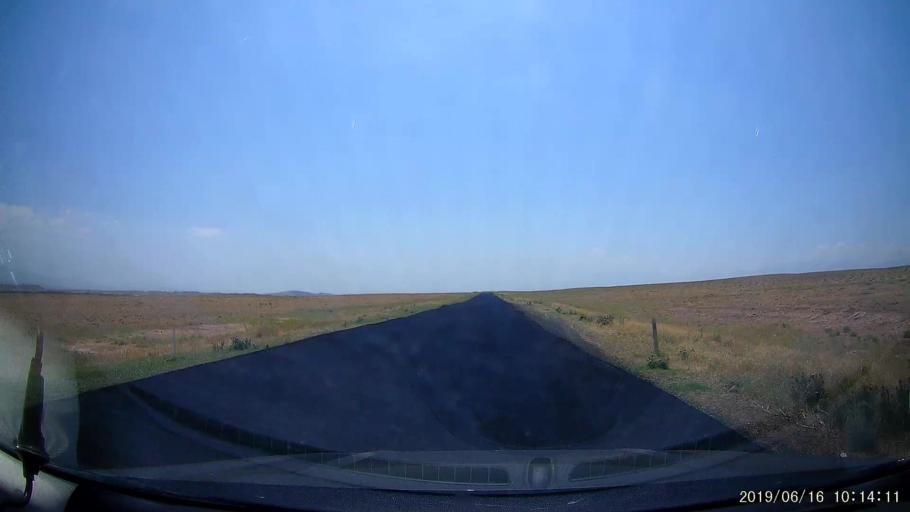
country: TR
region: Igdir
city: Tuzluca
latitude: 40.1871
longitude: 43.6573
